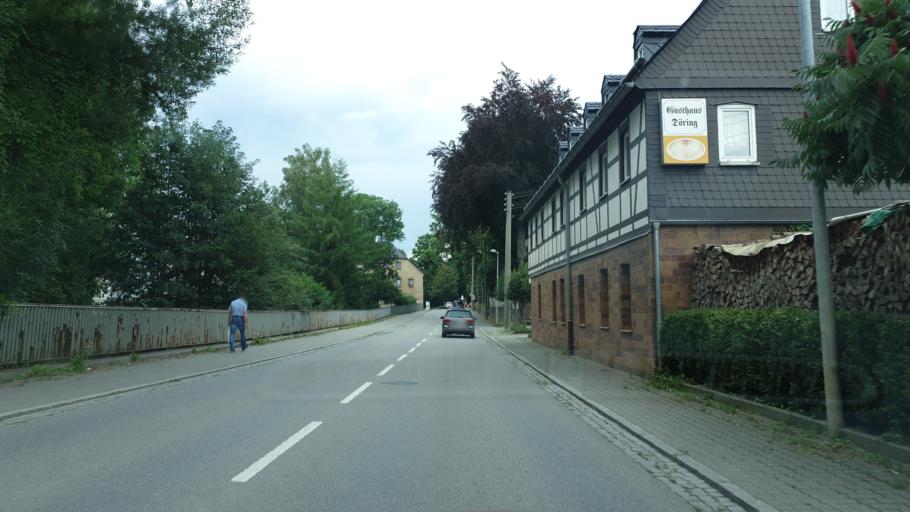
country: DE
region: Saxony
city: Zwonitz
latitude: 50.6423
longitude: 12.8202
